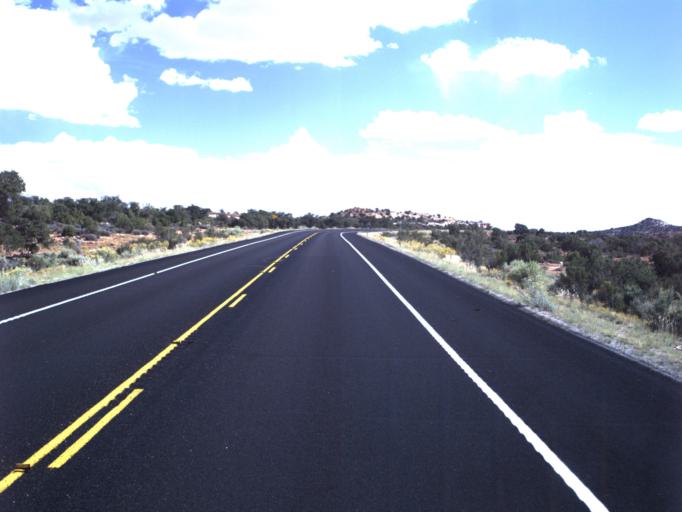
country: US
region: Utah
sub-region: Grand County
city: Moab
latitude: 38.5782
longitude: -109.7961
